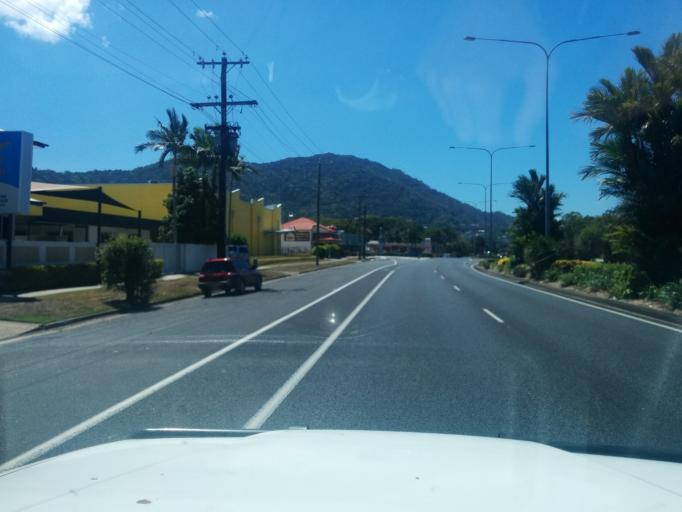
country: AU
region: Queensland
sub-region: Cairns
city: Woree
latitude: -16.9487
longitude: 145.7406
